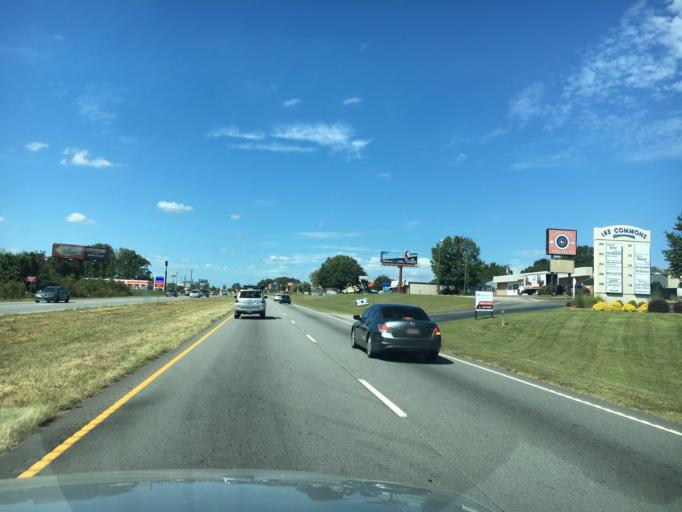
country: US
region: South Carolina
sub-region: Anderson County
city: Powdersville
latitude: 34.7839
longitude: -82.4755
